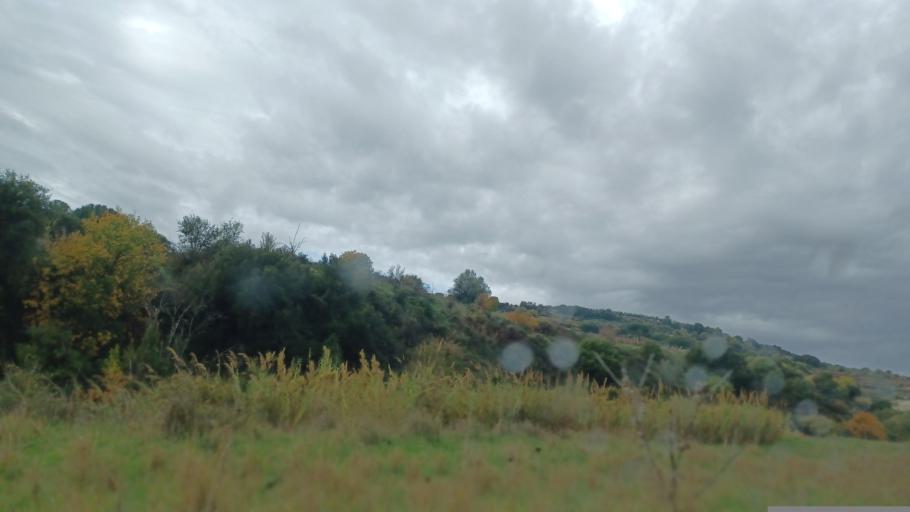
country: CY
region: Pafos
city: Mesogi
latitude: 34.8660
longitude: 32.5357
